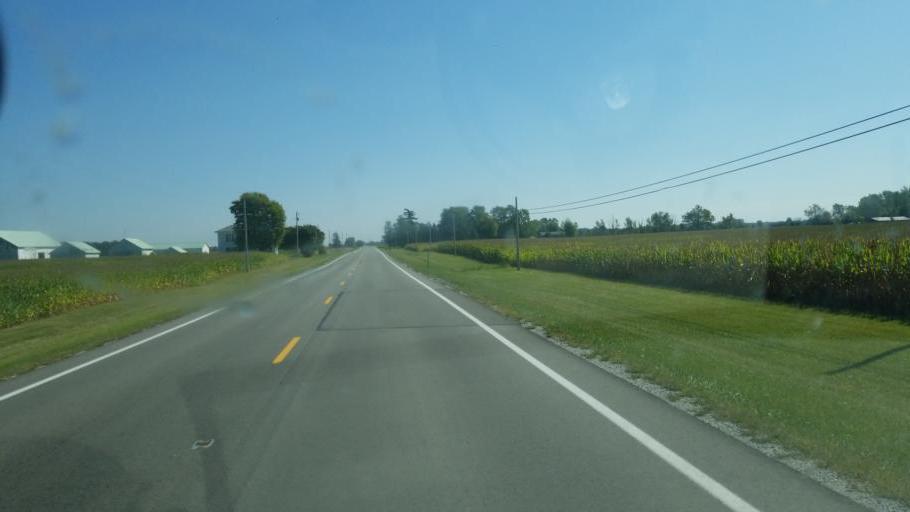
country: US
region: Ohio
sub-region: Hardin County
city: Kenton
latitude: 40.6429
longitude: -83.4955
